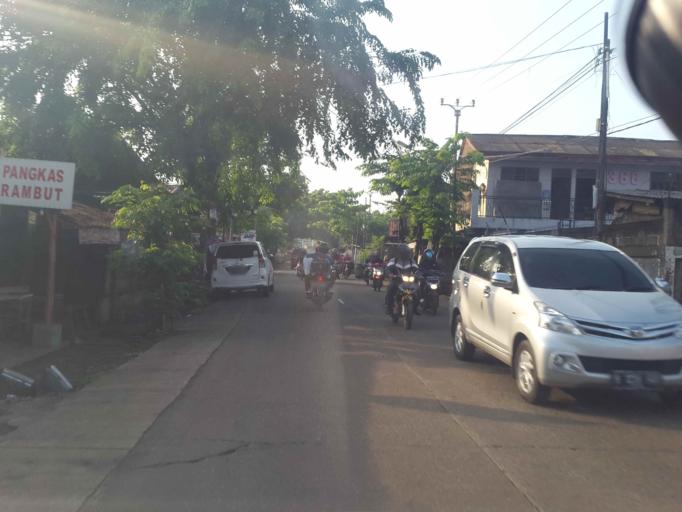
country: ID
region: West Java
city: Cikarang
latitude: -6.3018
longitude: 107.0665
